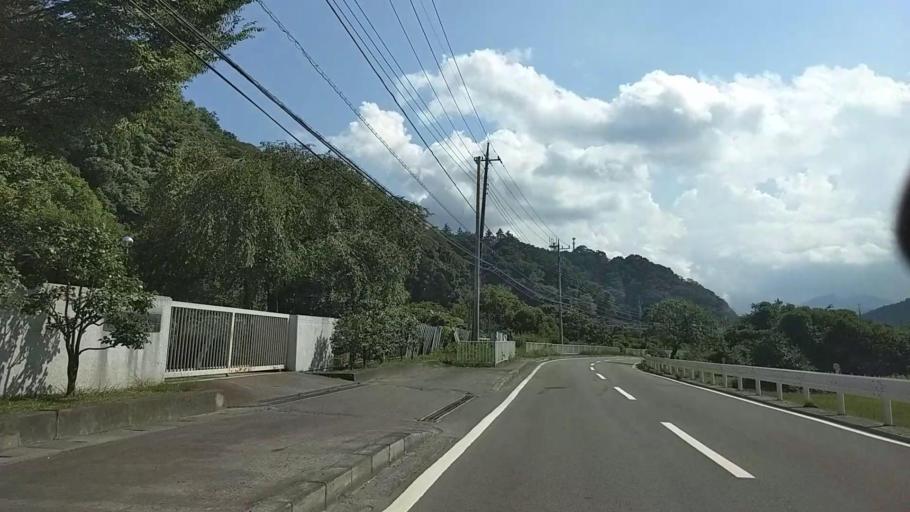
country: JP
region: Shizuoka
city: Fujinomiya
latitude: 35.3822
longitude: 138.4547
